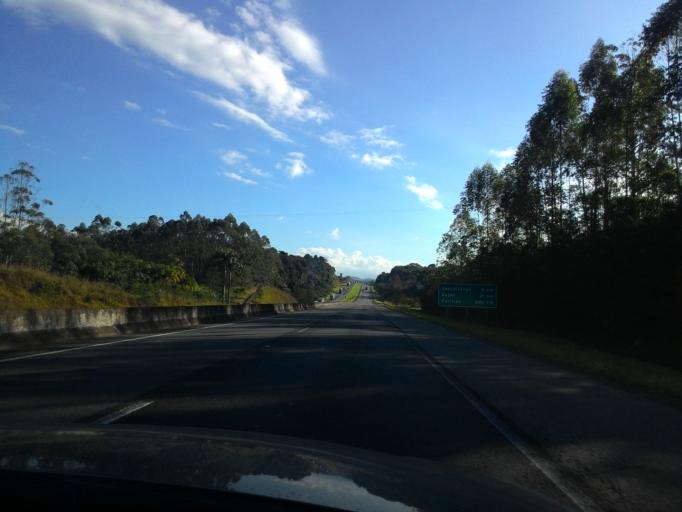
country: BR
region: Sao Paulo
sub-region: Pariquera-Acu
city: Pariquera Acu
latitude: -24.6491
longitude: -47.9308
